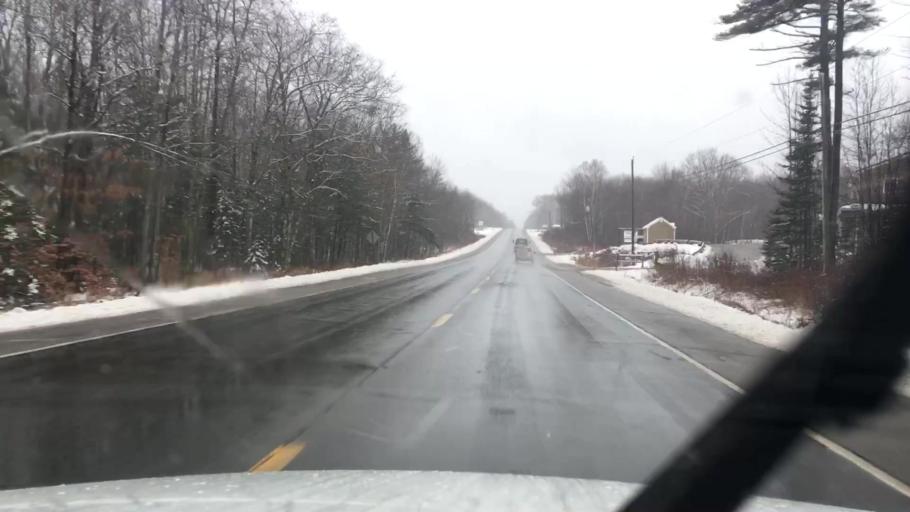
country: US
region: Maine
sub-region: Knox County
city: Warren
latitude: 44.1478
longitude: -69.1949
